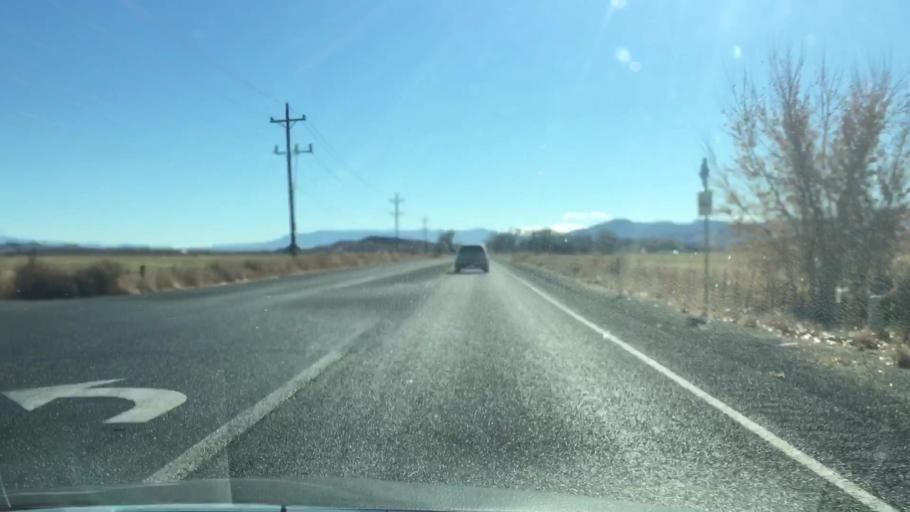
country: US
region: Nevada
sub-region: Lyon County
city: Yerington
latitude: 39.0482
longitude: -119.1815
